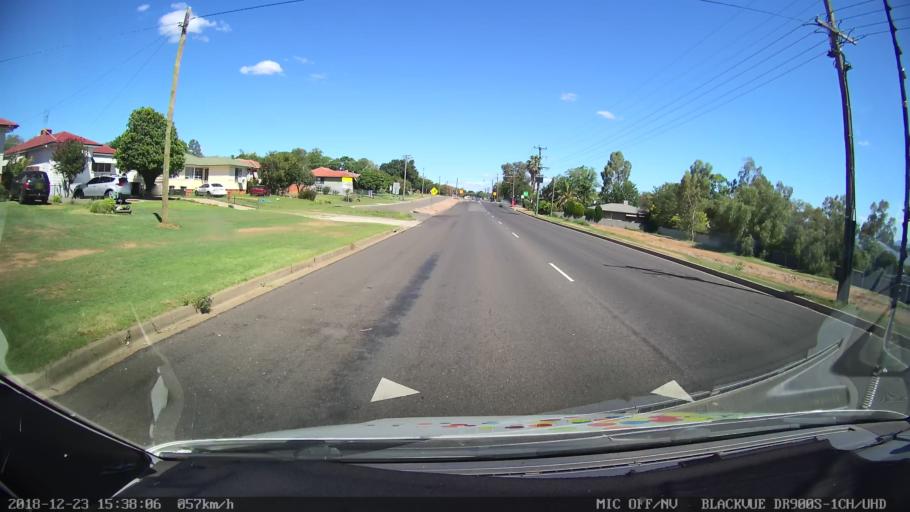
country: AU
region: New South Wales
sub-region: Tamworth Municipality
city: Tamworth
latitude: -31.0567
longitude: 150.8943
